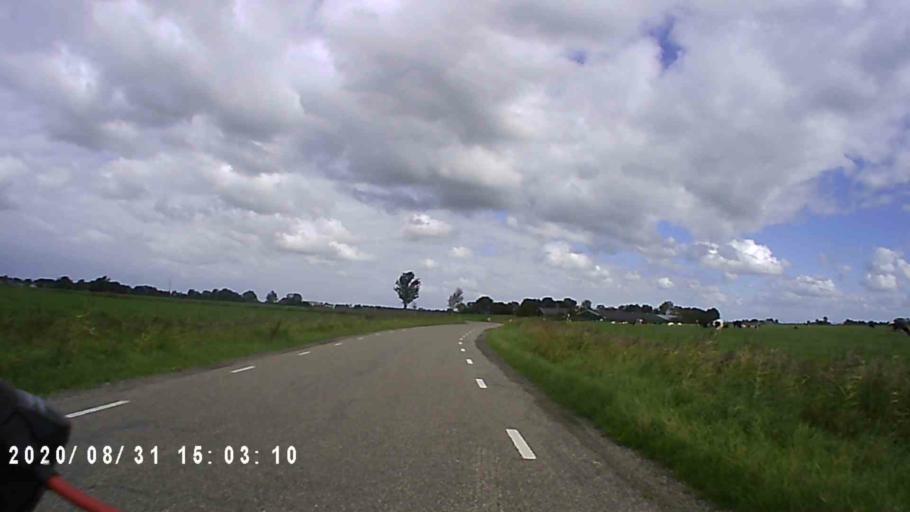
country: NL
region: Groningen
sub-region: Gemeente Zuidhorn
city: Oldehove
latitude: 53.2926
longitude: 6.3928
